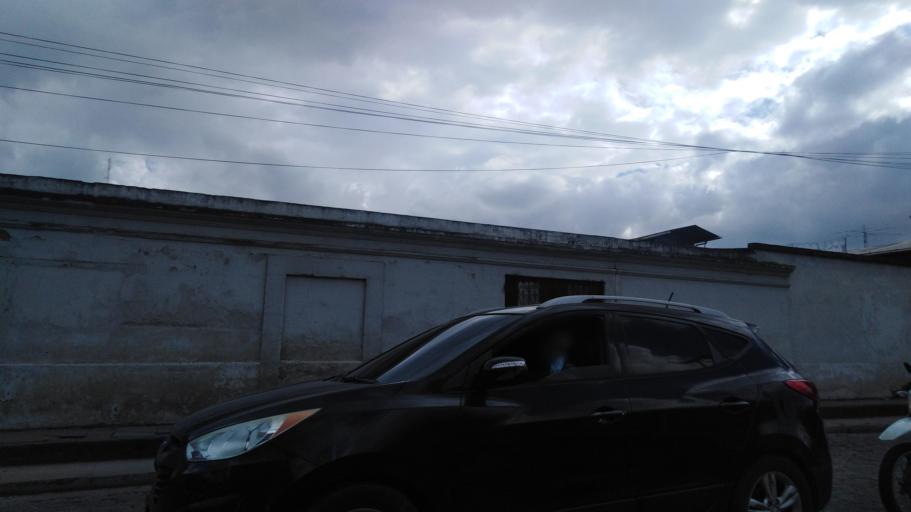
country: GT
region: Quetzaltenango
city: Quetzaltenango
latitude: 14.8466
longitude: -91.5173
